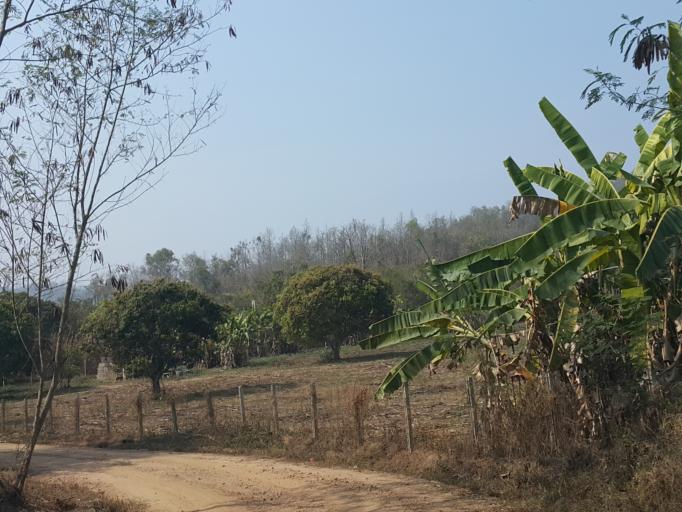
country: TH
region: Chiang Mai
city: Hang Dong
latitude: 18.7304
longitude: 98.8539
